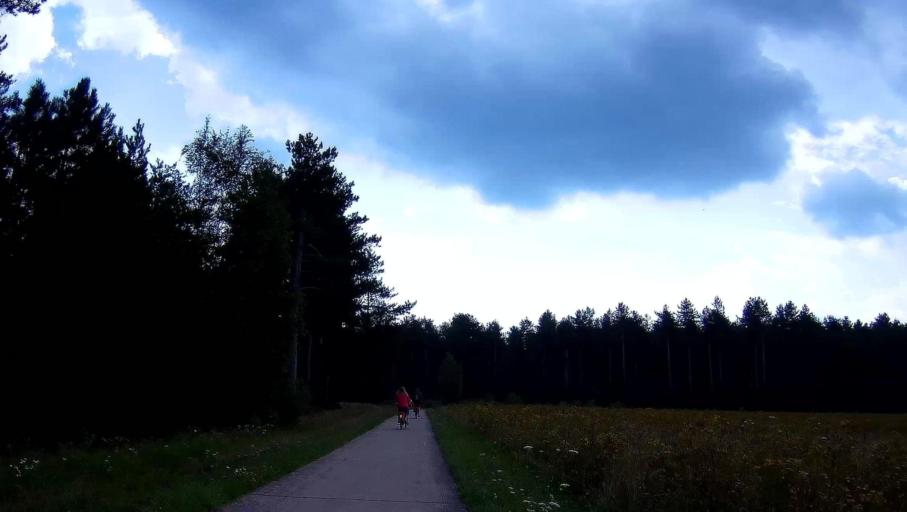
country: BE
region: Flanders
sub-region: Provincie Limburg
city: Lommel
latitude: 51.1861
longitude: 5.3282
